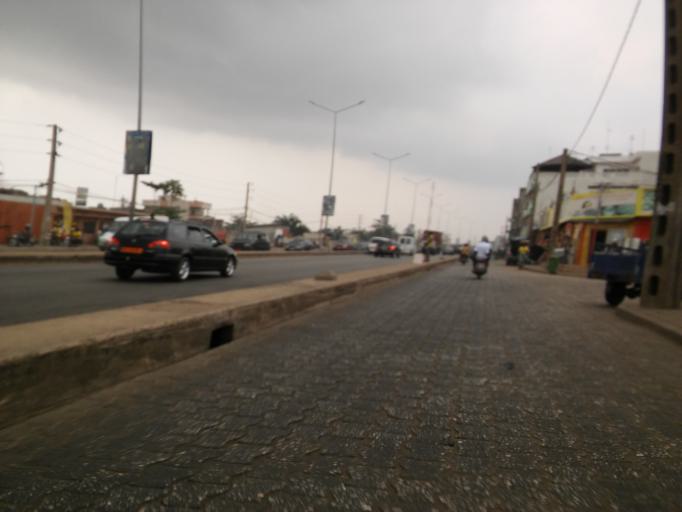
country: BJ
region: Littoral
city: Cotonou
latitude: 6.3775
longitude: 2.3846
